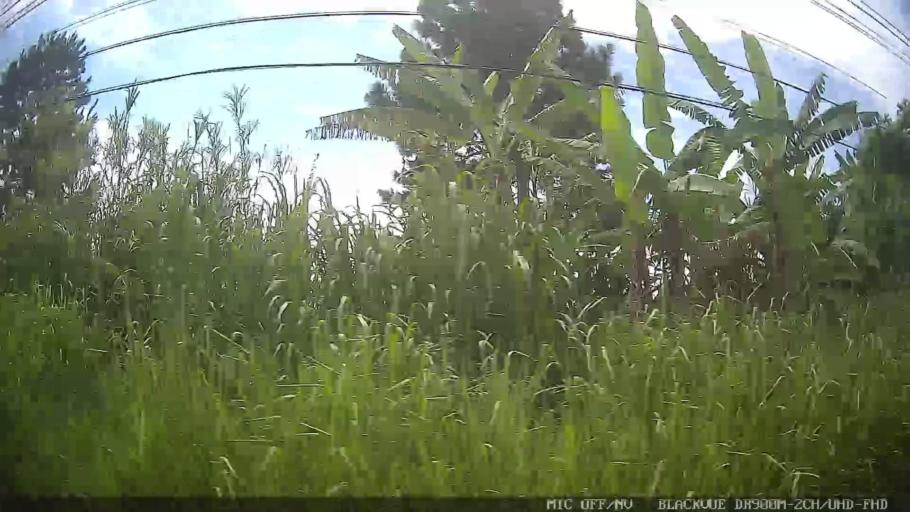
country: BR
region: Sao Paulo
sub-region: Santa Isabel
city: Santa Isabel
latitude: -23.4045
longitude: -46.2004
